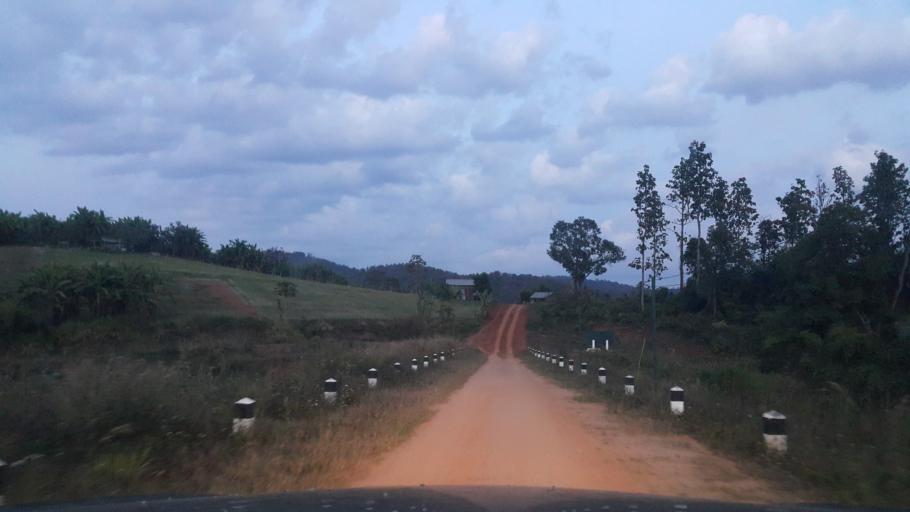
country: TH
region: Chiang Mai
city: Samoeng
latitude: 18.9532
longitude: 98.6724
